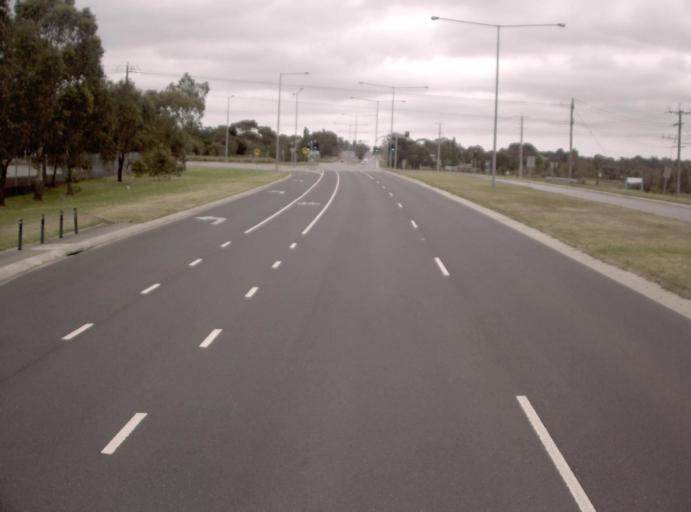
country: AU
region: Victoria
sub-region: Casey
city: Endeavour Hills
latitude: -37.9890
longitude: 145.2767
